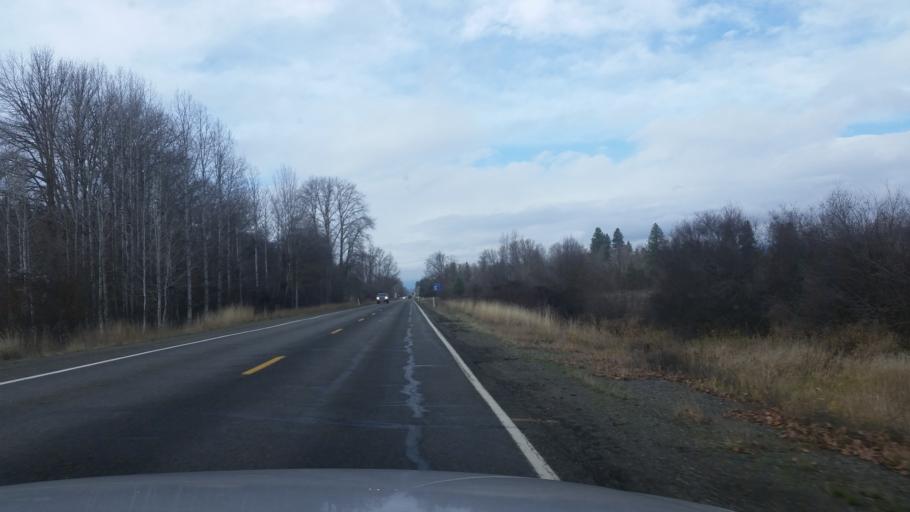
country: US
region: Washington
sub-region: Kittitas County
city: Cle Elum
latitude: 47.1674
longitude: -120.8302
